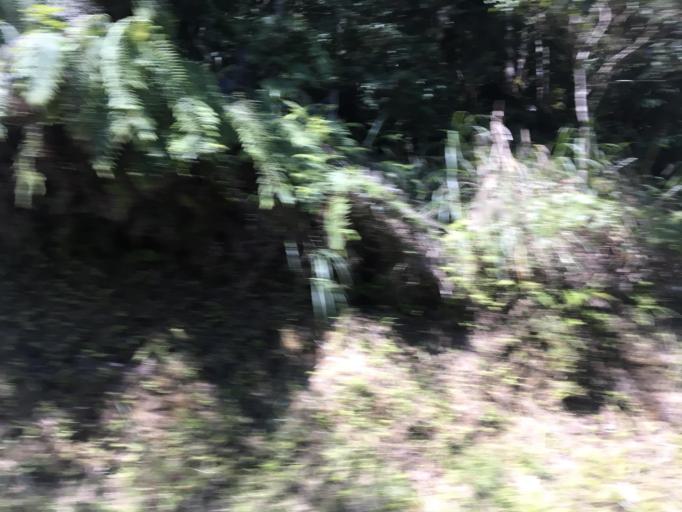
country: TW
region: Taiwan
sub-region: Yilan
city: Yilan
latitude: 24.5185
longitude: 121.5218
